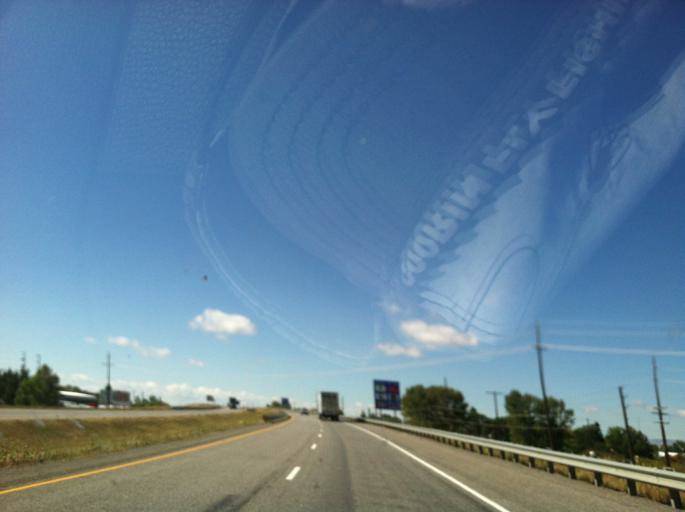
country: US
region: Montana
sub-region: Gallatin County
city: Bozeman
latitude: 45.6913
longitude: -111.0234
